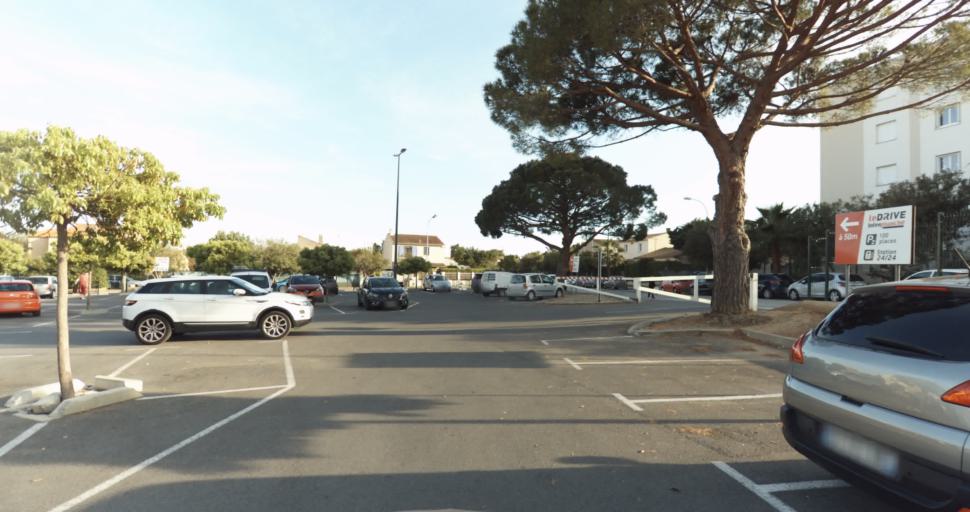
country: FR
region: Provence-Alpes-Cote d'Azur
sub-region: Departement du Var
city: Hyeres
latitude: 43.1235
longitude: 6.1471
